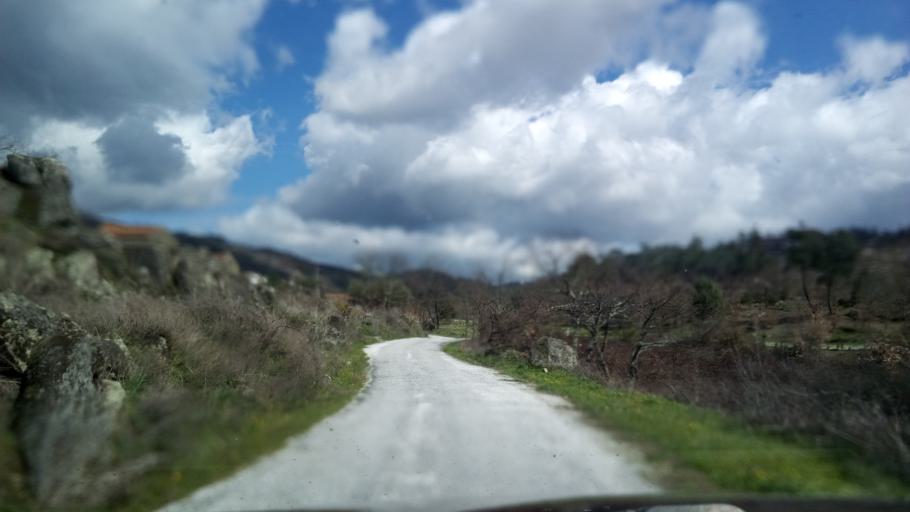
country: PT
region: Guarda
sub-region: Fornos de Algodres
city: Fornos de Algodres
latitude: 40.6525
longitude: -7.5003
